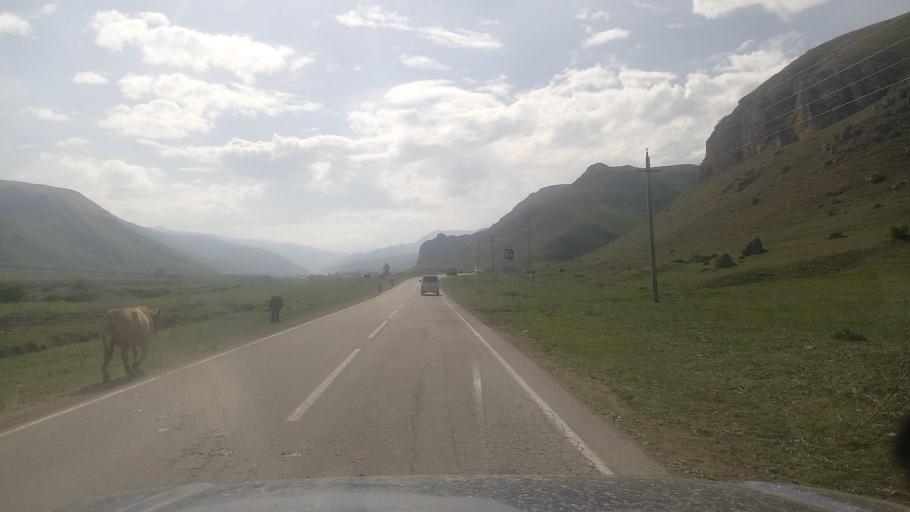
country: RU
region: Kabardino-Balkariya
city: Kamennomostskoye
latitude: 43.7344
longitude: 42.9759
